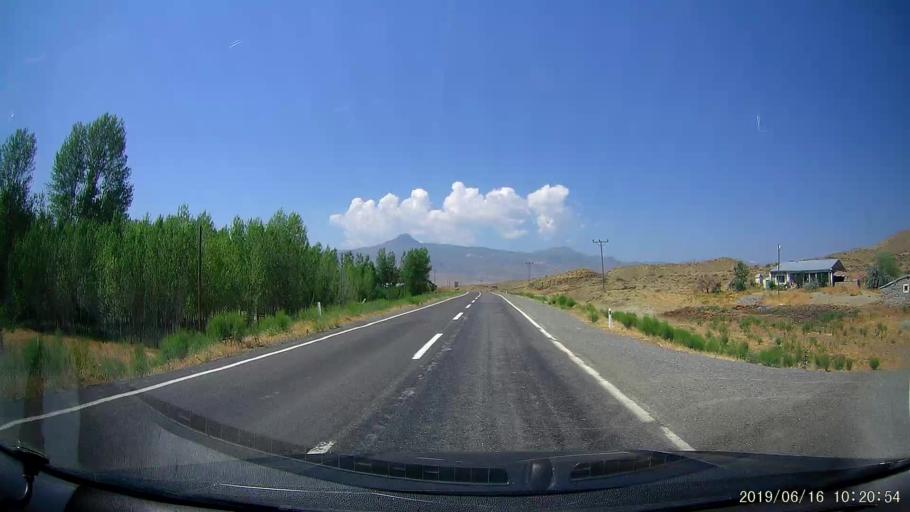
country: TR
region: Igdir
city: Tuzluca
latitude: 40.1434
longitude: 43.6428
